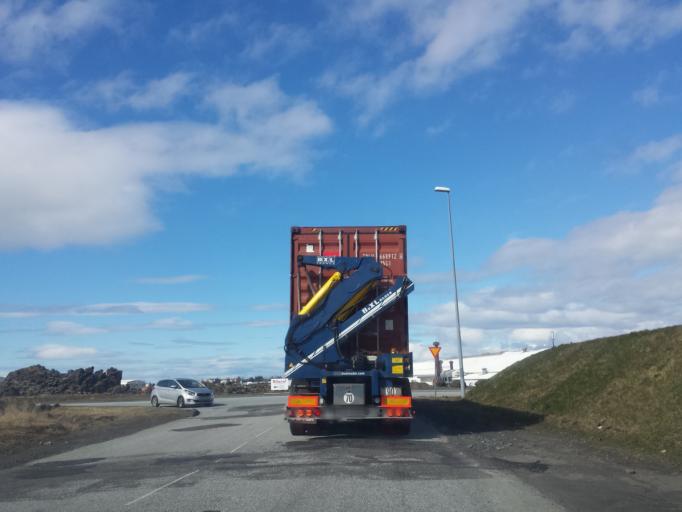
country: IS
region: Capital Region
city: Gardabaer
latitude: 64.0772
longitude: -21.9286
